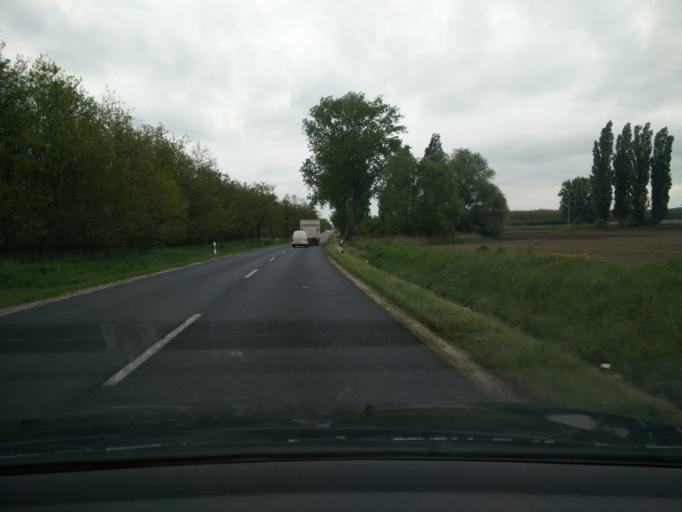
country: HU
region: Gyor-Moson-Sopron
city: Gyorszemere
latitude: 47.5382
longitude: 17.5370
